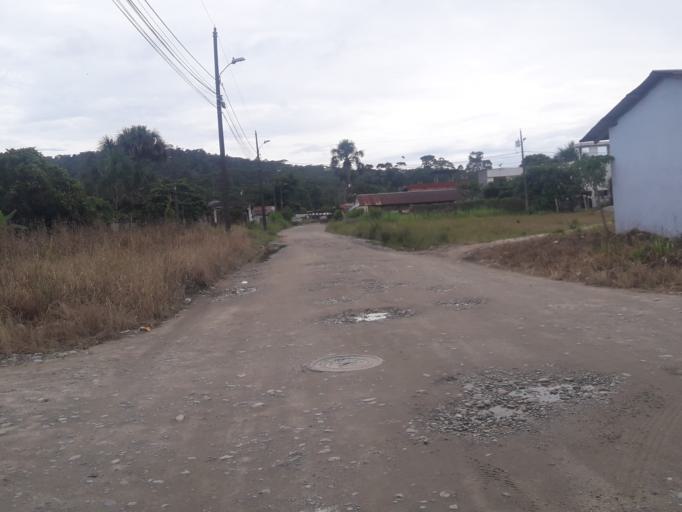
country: EC
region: Napo
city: Tena
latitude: -0.9877
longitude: -77.8310
